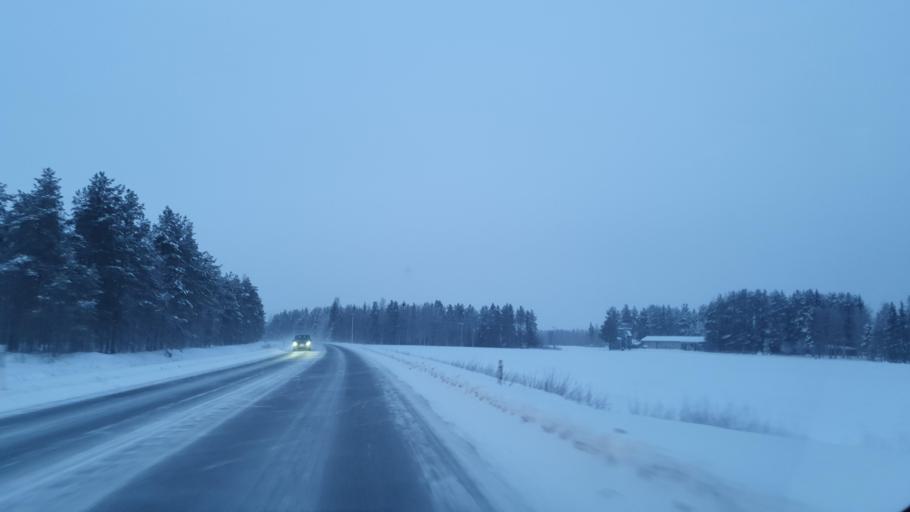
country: FI
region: Northern Ostrobothnia
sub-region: Oulunkaari
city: Utajaervi
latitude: 64.7157
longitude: 26.5131
